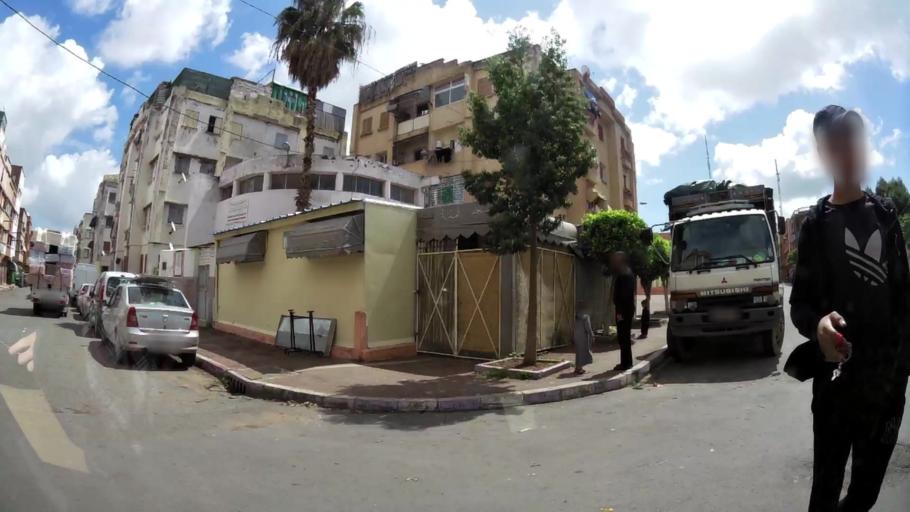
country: MA
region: Grand Casablanca
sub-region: Casablanca
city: Casablanca
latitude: 33.5404
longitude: -7.5855
